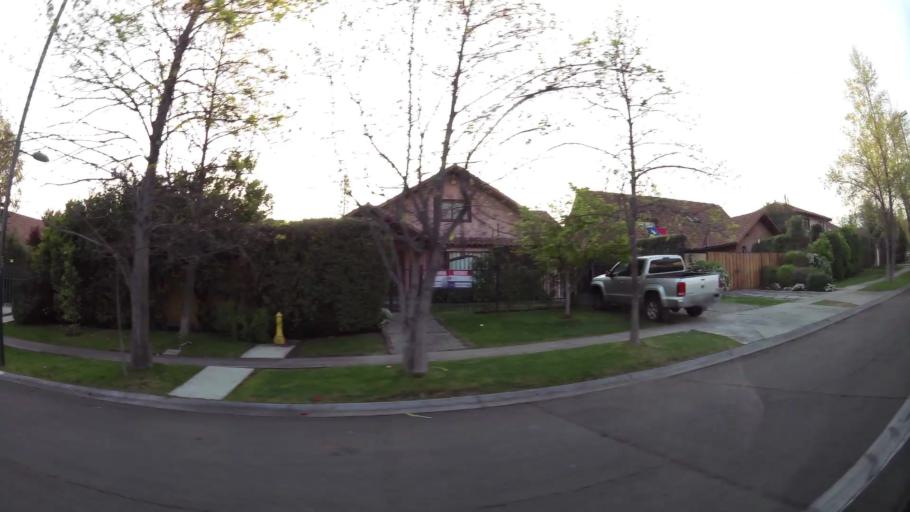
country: CL
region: Santiago Metropolitan
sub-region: Provincia de Chacabuco
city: Chicureo Abajo
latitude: -33.3276
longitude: -70.5386
